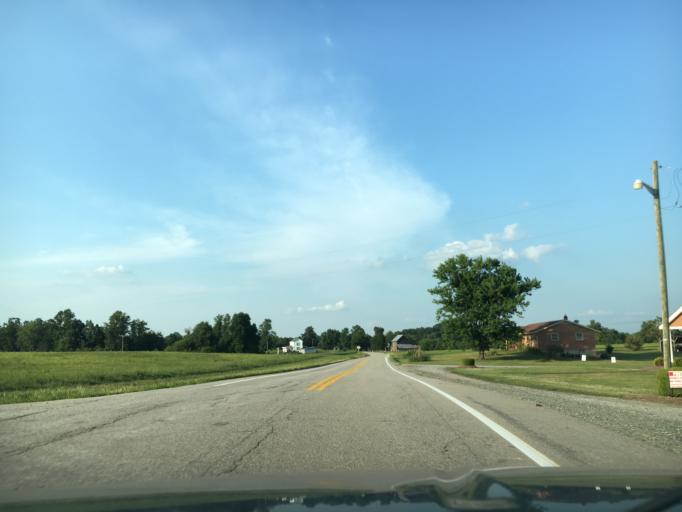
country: US
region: Virginia
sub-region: Pittsylvania County
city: Chatham
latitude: 36.8402
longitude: -79.2242
